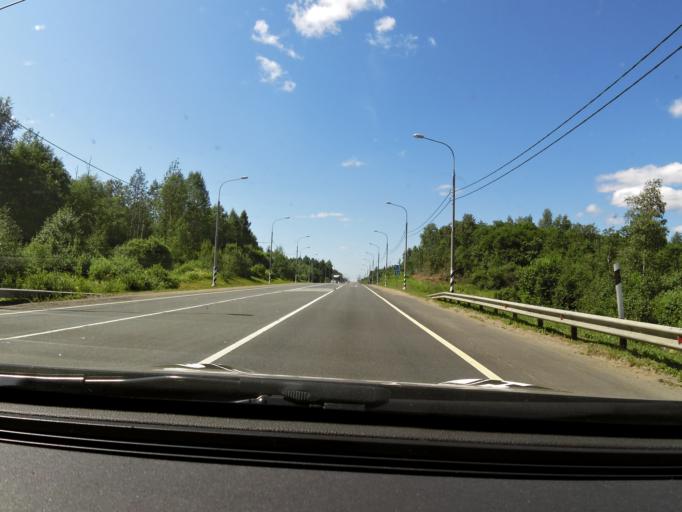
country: RU
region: Novgorod
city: Valday
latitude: 57.9928
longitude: 33.1888
